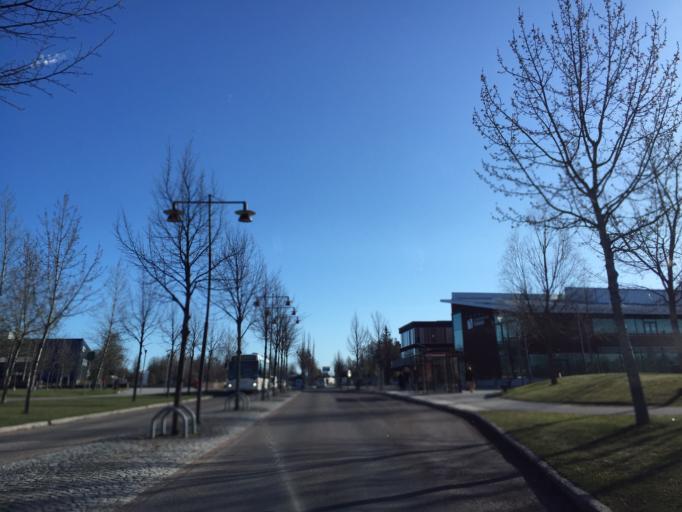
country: SE
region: Dalarna
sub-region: Borlange Kommun
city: Borlaenge
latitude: 60.4854
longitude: 15.4095
